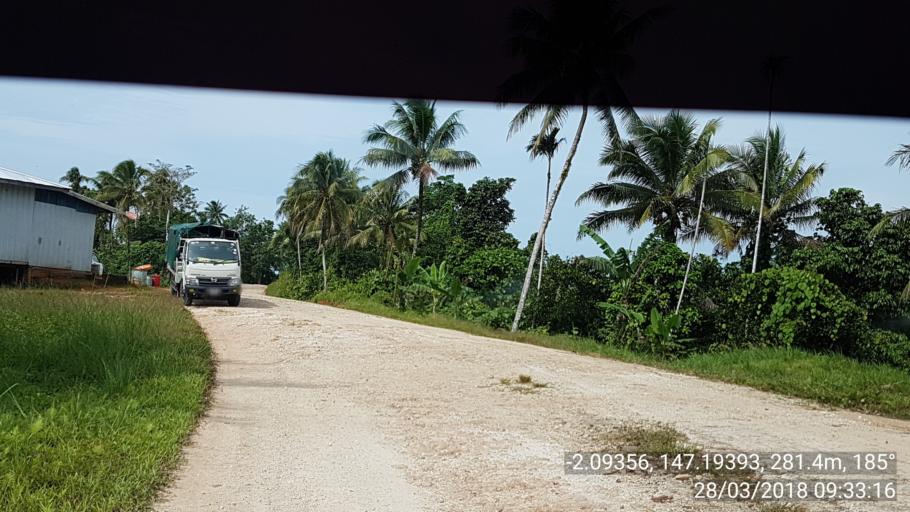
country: PG
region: Manus
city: Lorengau
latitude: -2.0936
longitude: 147.1939
